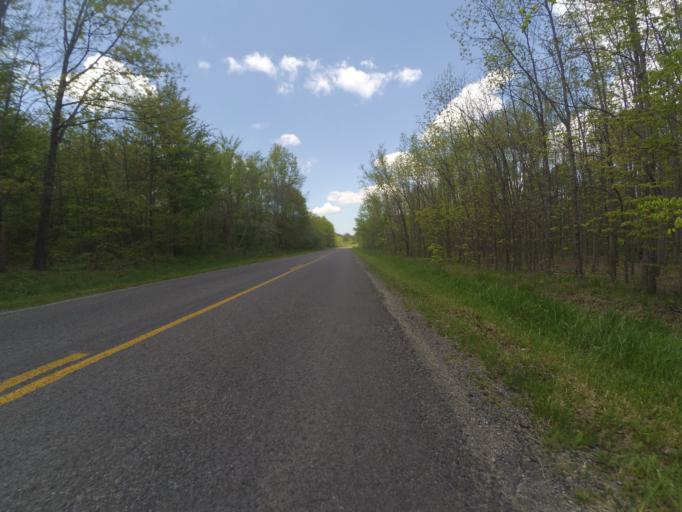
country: US
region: Ohio
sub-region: Mahoning County
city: Craig Beach
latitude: 41.1301
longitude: -81.0986
